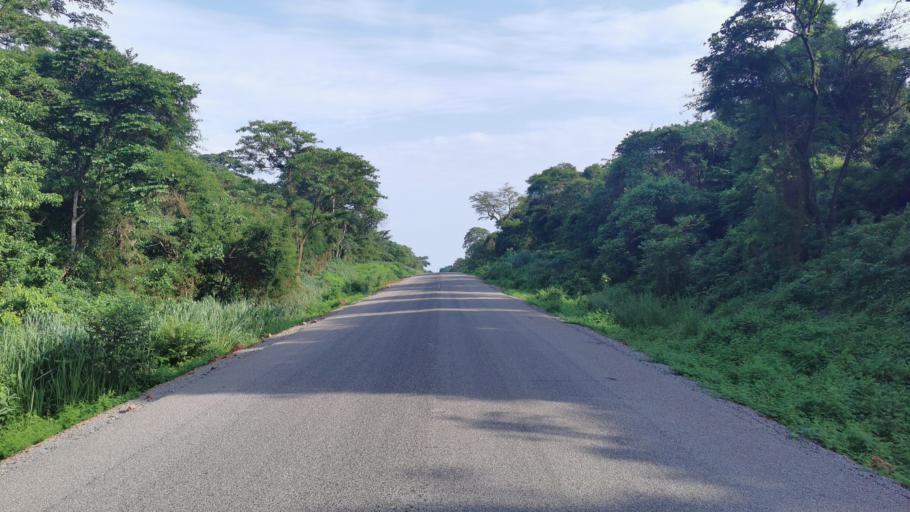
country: ET
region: Gambela
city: Gambela
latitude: 7.7507
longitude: 34.6617
